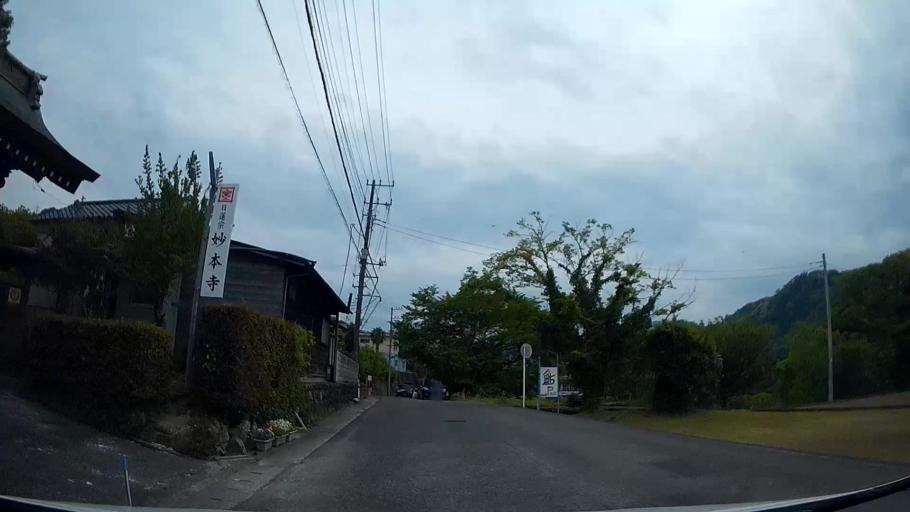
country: JP
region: Shizuoka
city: Ito
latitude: 34.9469
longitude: 138.9366
